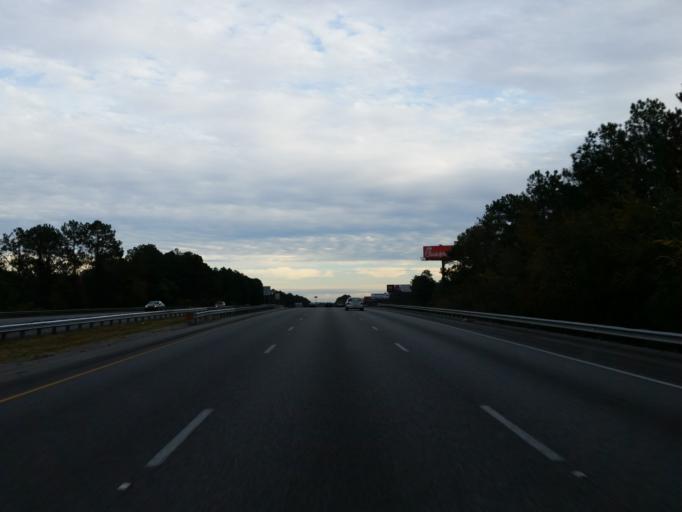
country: US
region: Georgia
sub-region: Lowndes County
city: Valdosta
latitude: 30.7726
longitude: -83.2928
